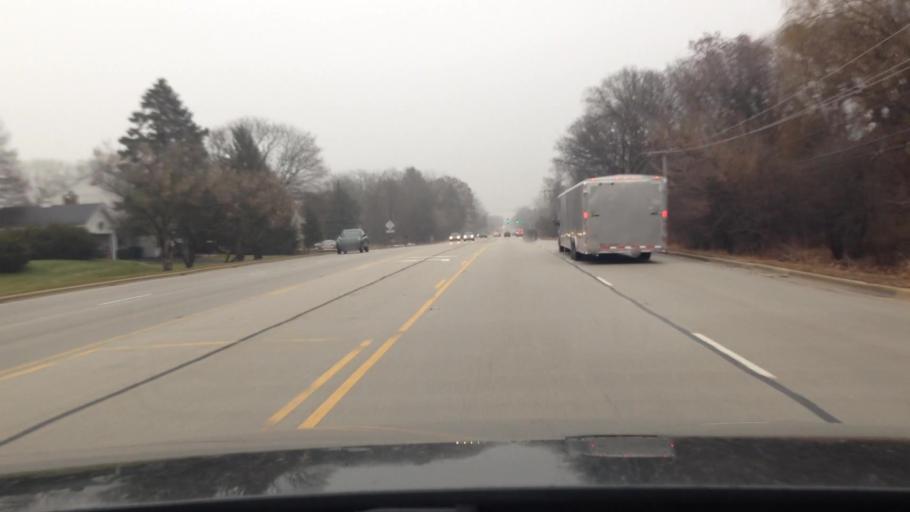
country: US
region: Illinois
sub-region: DuPage County
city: Downers Grove
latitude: 41.8314
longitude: -87.9958
